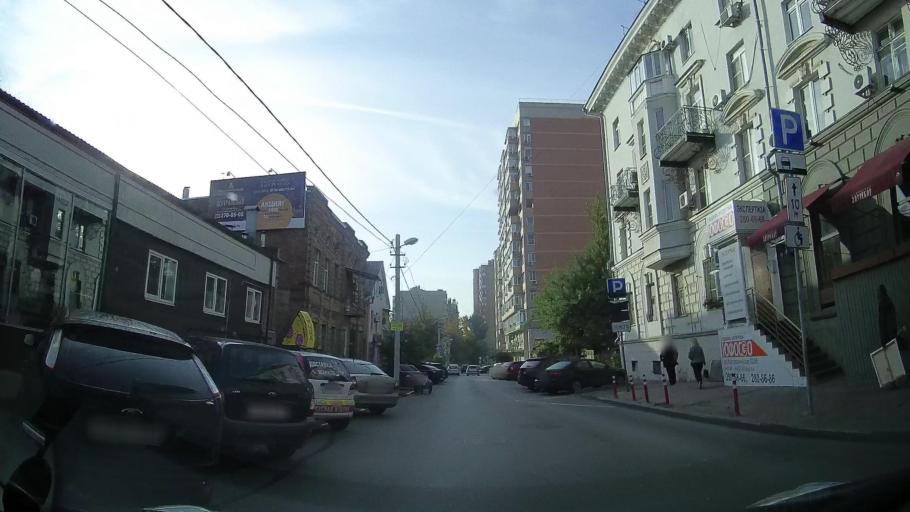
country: RU
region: Rostov
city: Rostov-na-Donu
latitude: 47.2249
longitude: 39.6999
